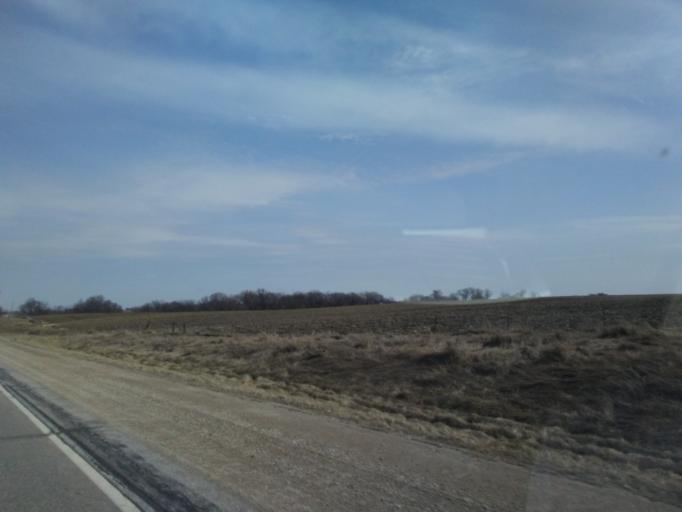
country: US
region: Iowa
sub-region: Allamakee County
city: Waukon
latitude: 43.2407
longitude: -91.5853
